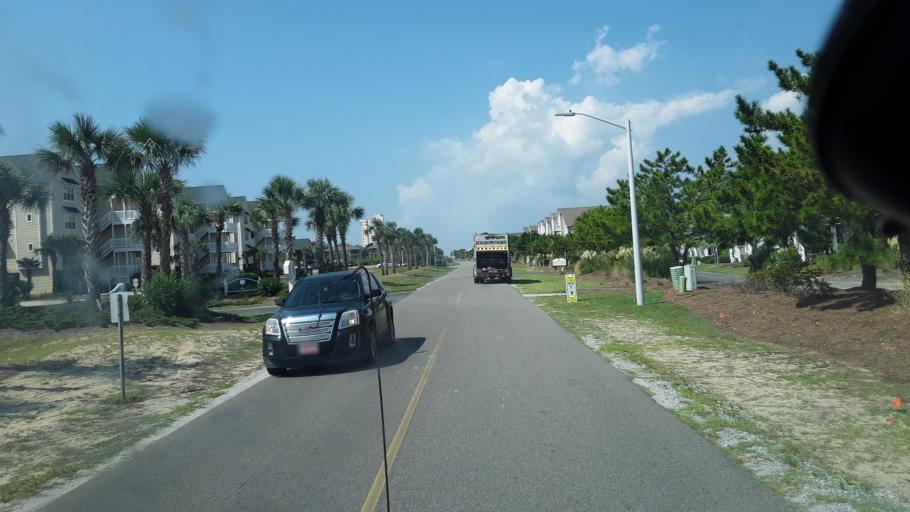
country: US
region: North Carolina
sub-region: Brunswick County
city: Sunset Beach
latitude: 33.8811
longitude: -78.4633
